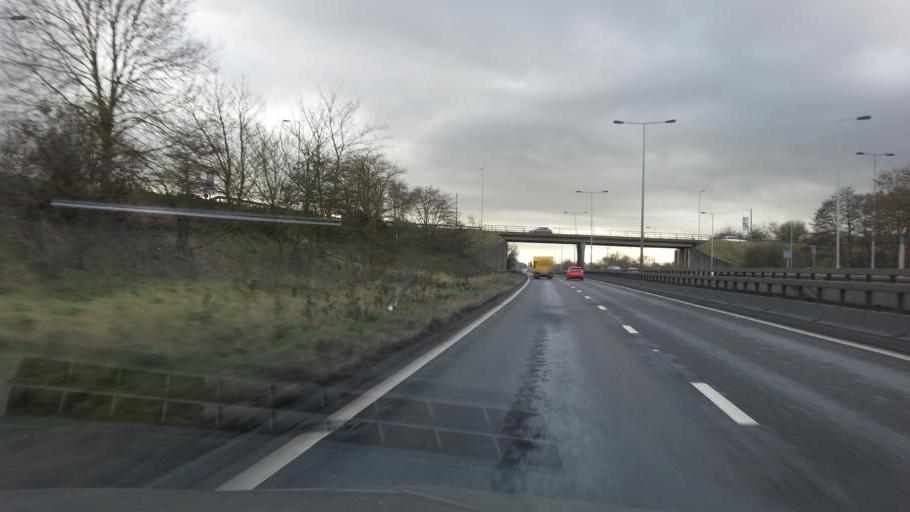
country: GB
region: England
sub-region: Staffordshire
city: Alrewas
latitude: 52.7275
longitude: -1.7453
